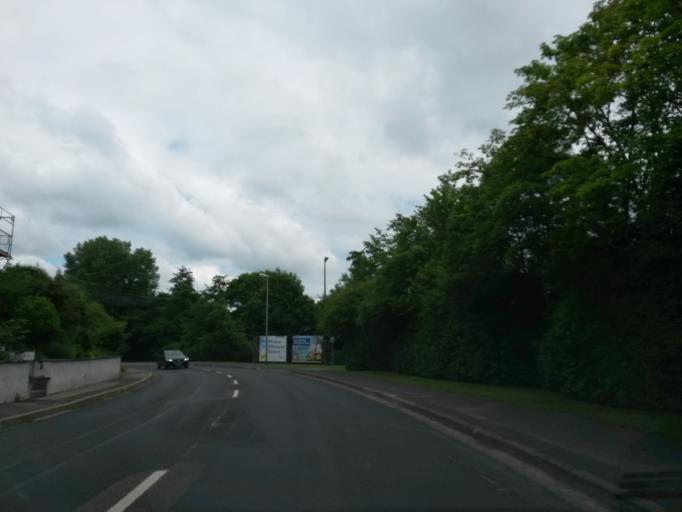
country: DE
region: Bavaria
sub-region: Regierungsbezirk Unterfranken
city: Rimpar
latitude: 49.8511
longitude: 9.9590
